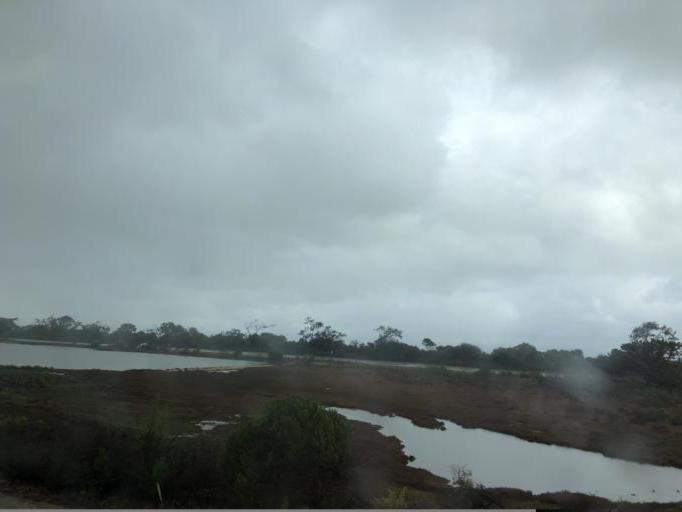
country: US
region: California
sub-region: San Mateo County
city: Brisbane
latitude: 37.6768
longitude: -122.3902
